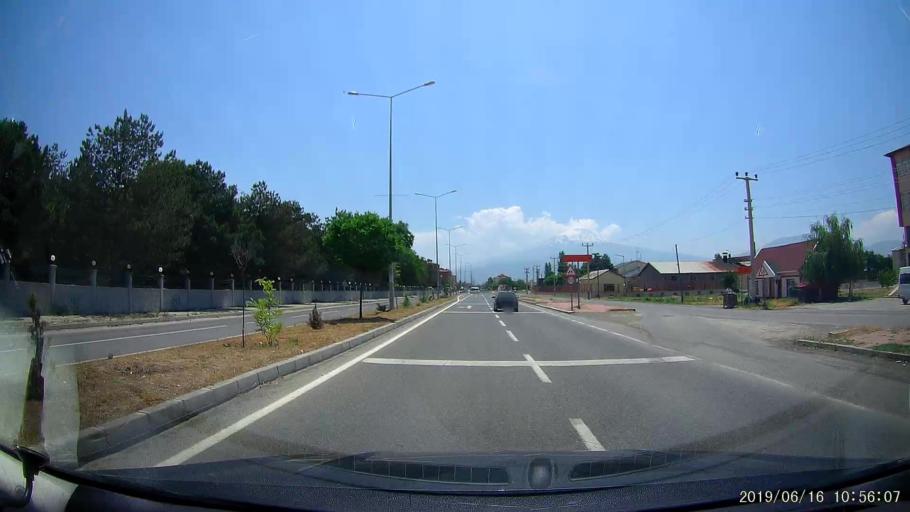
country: TR
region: Igdir
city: Igdir
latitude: 39.9321
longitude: 44.0182
